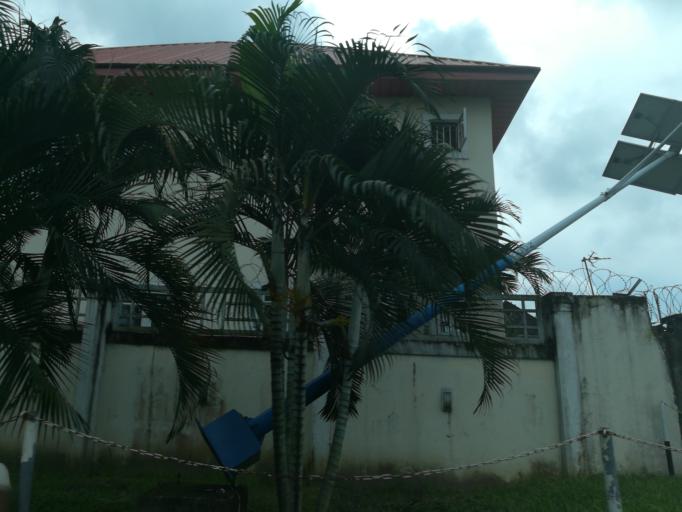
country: NG
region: Rivers
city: Port Harcourt
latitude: 4.8101
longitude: 6.9913
